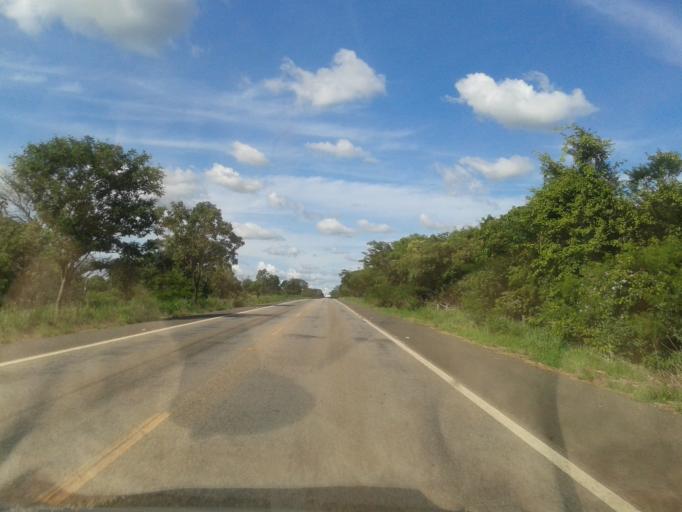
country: BR
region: Goias
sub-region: Mozarlandia
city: Mozarlandia
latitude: -15.0610
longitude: -50.6139
